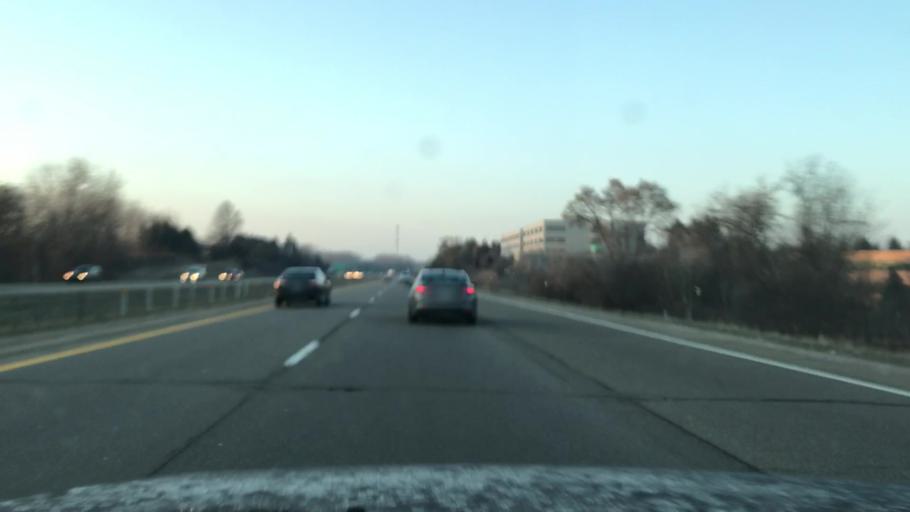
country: US
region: Michigan
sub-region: Kent County
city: East Grand Rapids
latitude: 42.9426
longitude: -85.5668
